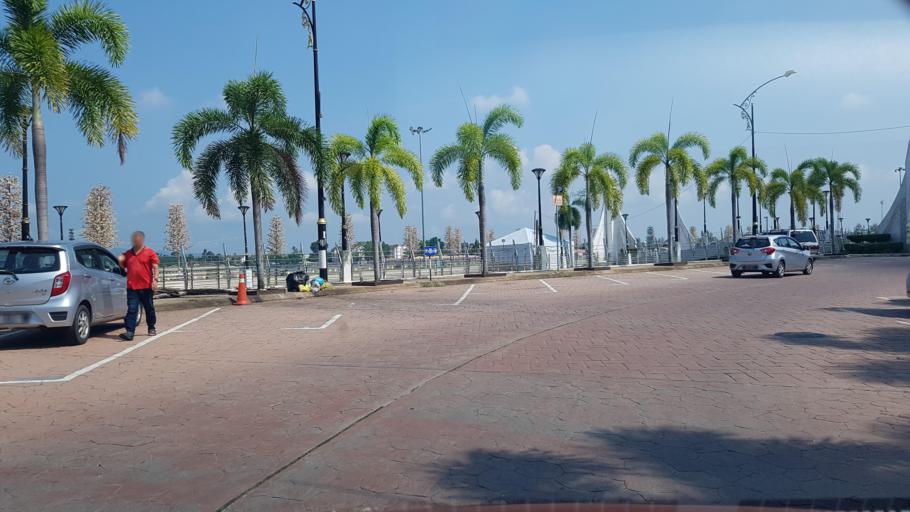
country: MY
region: Terengganu
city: Kuala Terengganu
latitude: 5.3315
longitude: 103.1320
